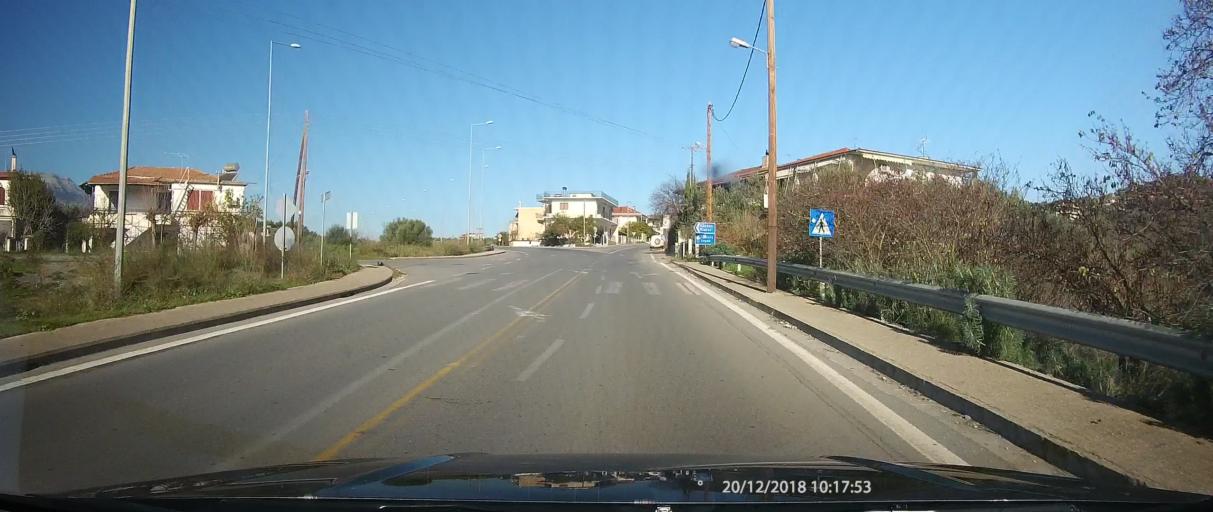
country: GR
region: Peloponnese
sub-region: Nomos Lakonias
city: Sparti
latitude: 37.1116
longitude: 22.4325
